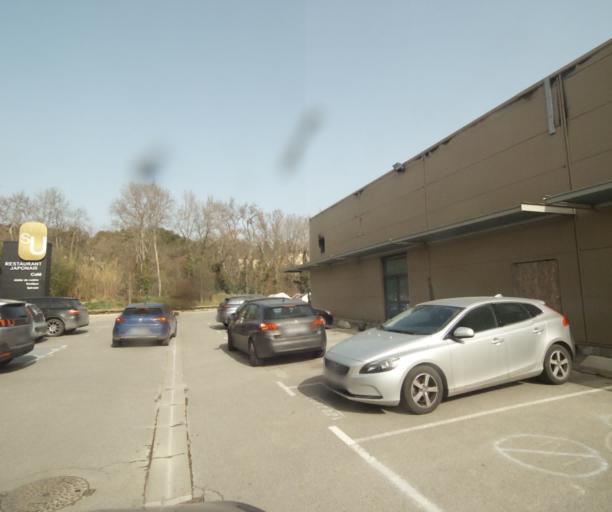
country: FR
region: Provence-Alpes-Cote d'Azur
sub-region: Departement des Bouches-du-Rhone
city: Aix-en-Provence
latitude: 43.5088
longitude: 5.4028
